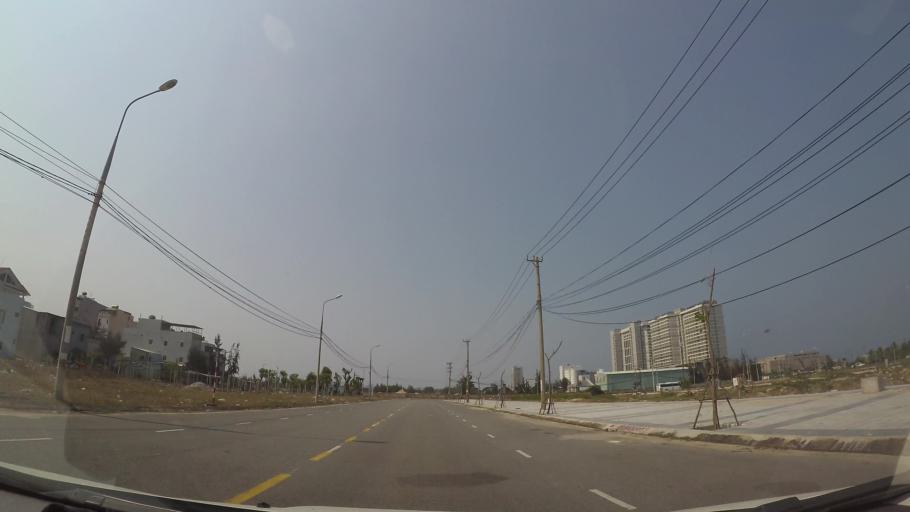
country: VN
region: Da Nang
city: Ngu Hanh Son
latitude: 16.0196
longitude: 108.2567
